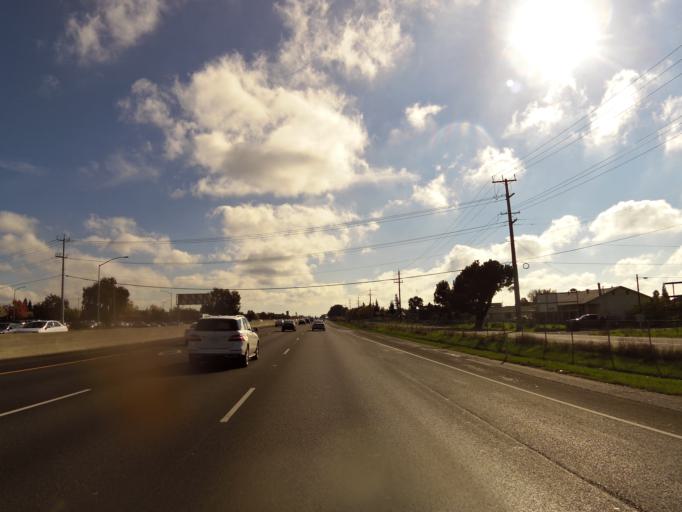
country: US
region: California
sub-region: Sacramento County
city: Laguna
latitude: 38.4532
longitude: -121.4091
